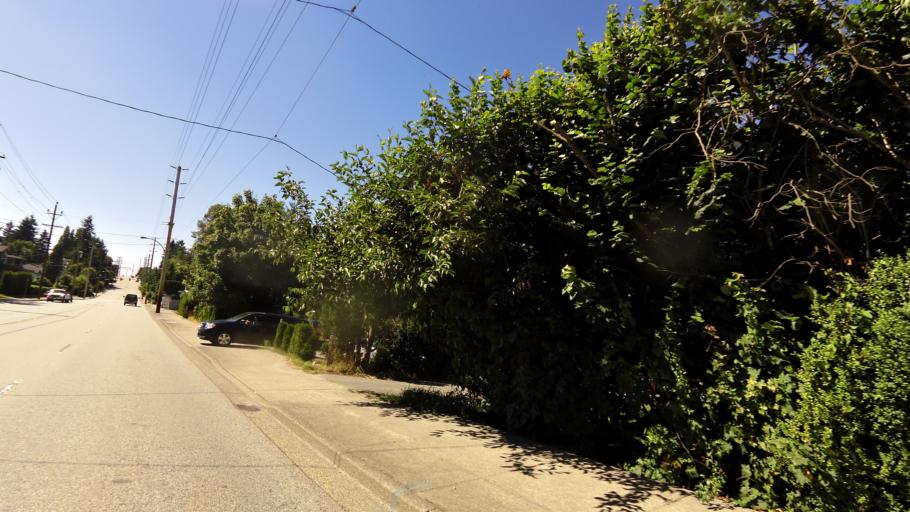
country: CA
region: British Columbia
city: Port Moody
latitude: 49.2636
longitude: -122.8732
